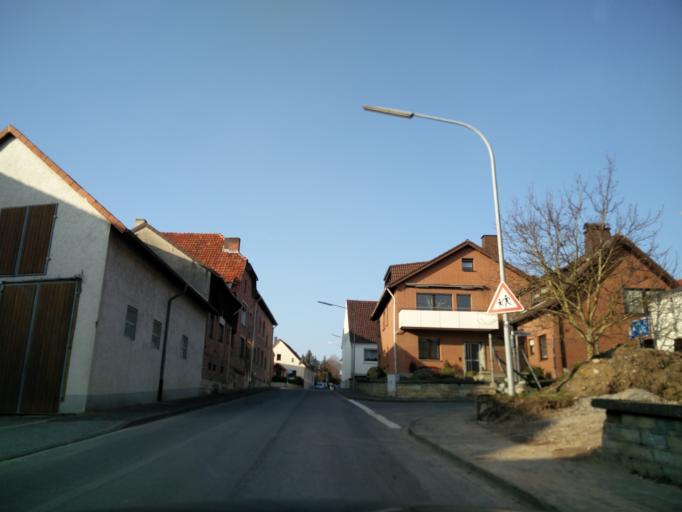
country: DE
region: North Rhine-Westphalia
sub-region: Regierungsbezirk Detmold
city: Paderborn
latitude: 51.6528
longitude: 8.7025
